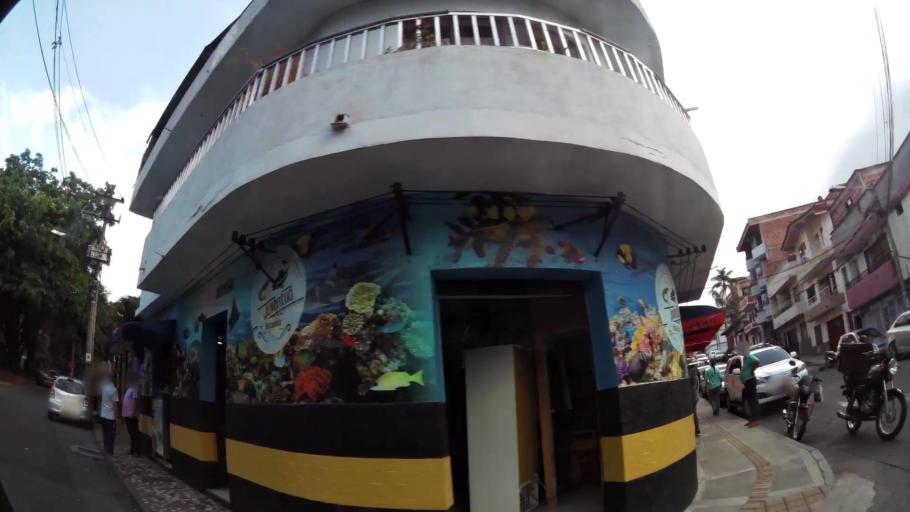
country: CO
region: Antioquia
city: Envigado
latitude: 6.1688
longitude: -75.5833
